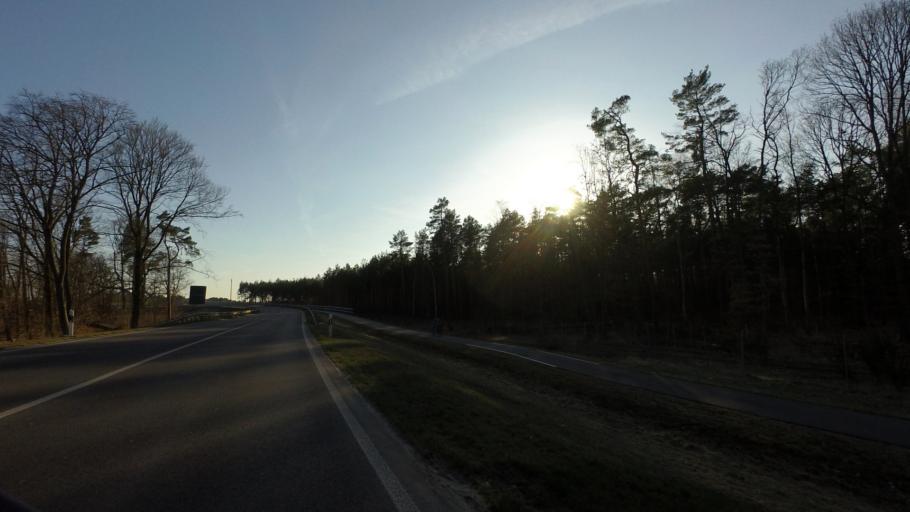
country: DE
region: Brandenburg
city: Eberswalde
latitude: 52.8597
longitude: 13.8316
